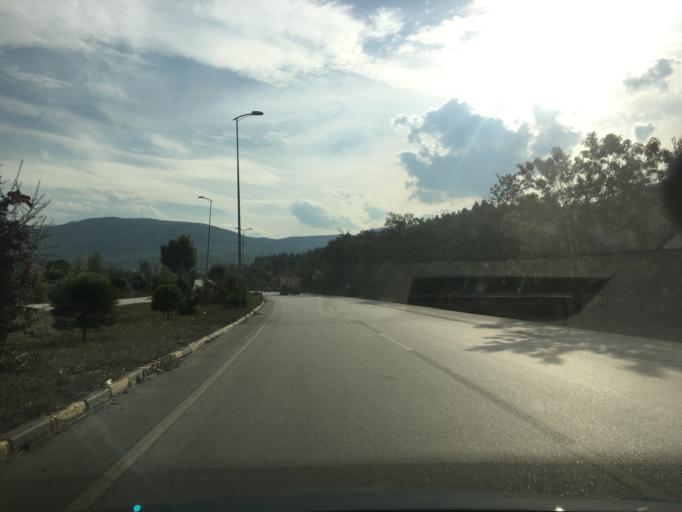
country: TR
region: Karabuk
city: Karabuk
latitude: 41.1185
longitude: 32.6738
